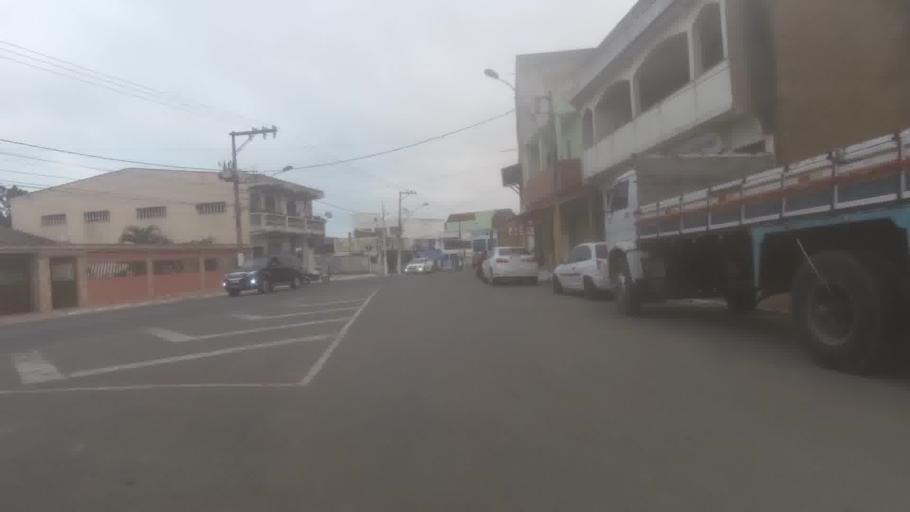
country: BR
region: Espirito Santo
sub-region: Marataizes
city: Marataizes
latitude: -21.0406
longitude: -40.8226
